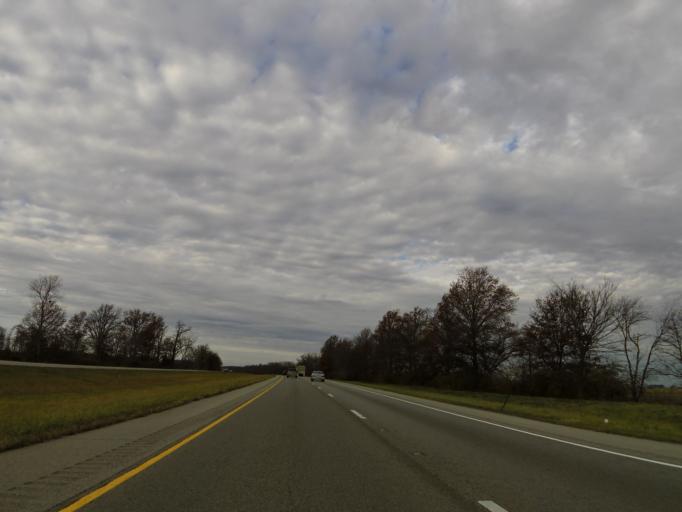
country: US
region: Illinois
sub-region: Clinton County
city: Wamac
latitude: 38.3861
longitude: -89.1290
